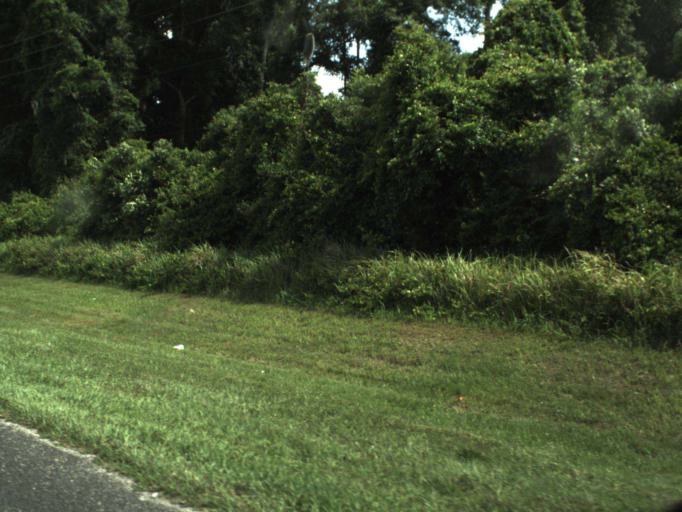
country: US
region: Florida
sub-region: Marion County
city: Ocala
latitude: 29.1523
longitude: -82.0783
